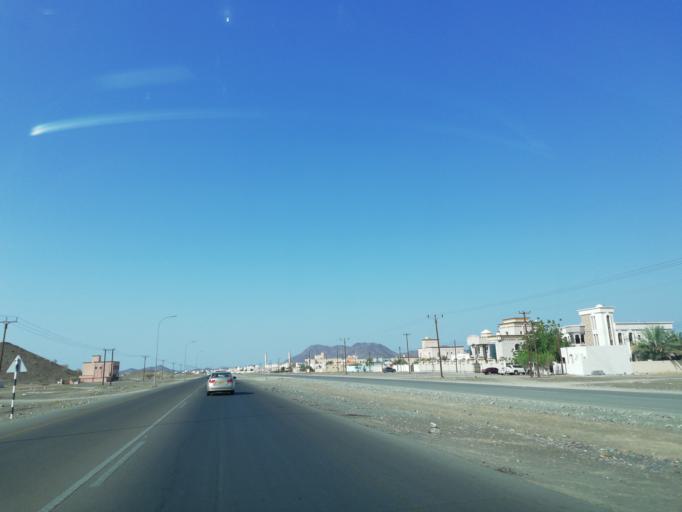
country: OM
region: Ash Sharqiyah
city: Ibra'
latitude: 22.7895
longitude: 58.1468
